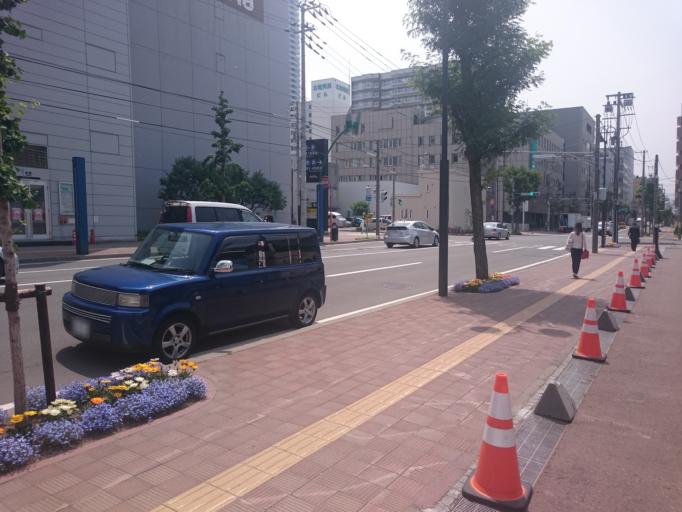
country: JP
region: Hokkaido
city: Sapporo
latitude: 43.0647
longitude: 141.3622
